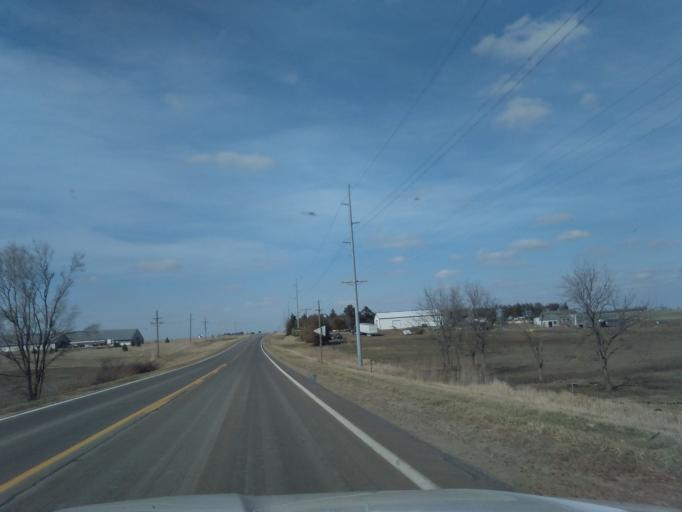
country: US
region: Nebraska
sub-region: Gage County
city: Beatrice
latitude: 40.1853
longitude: -96.9352
